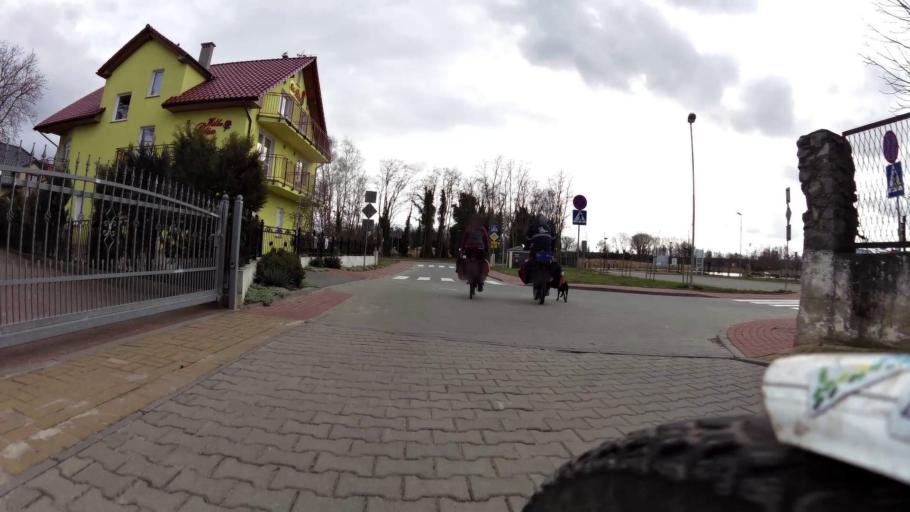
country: PL
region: West Pomeranian Voivodeship
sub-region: Powiat kamienski
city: Dziwnow
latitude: 54.0215
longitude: 14.7397
